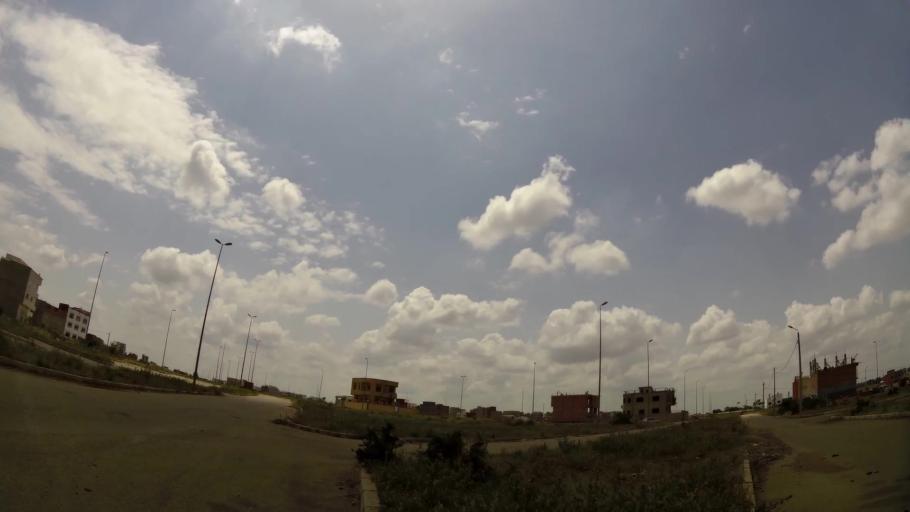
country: MA
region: Rabat-Sale-Zemmour-Zaer
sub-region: Khemisset
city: Tiflet
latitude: 34.0048
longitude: -6.5392
